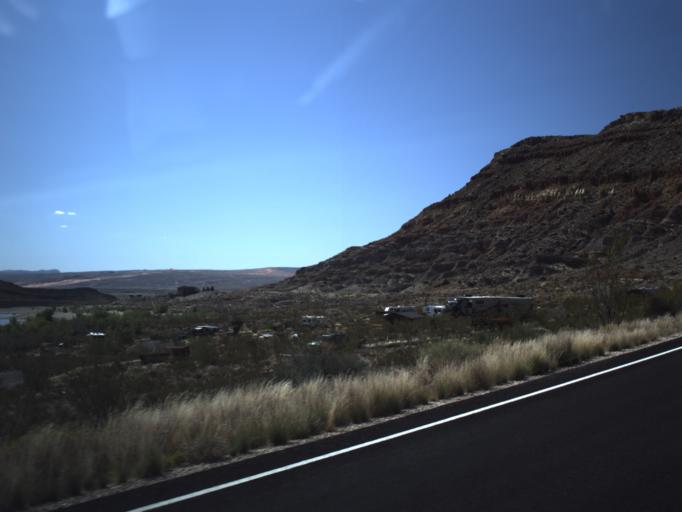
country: US
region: Utah
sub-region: Washington County
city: Hurricane
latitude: 37.1879
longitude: -113.3953
